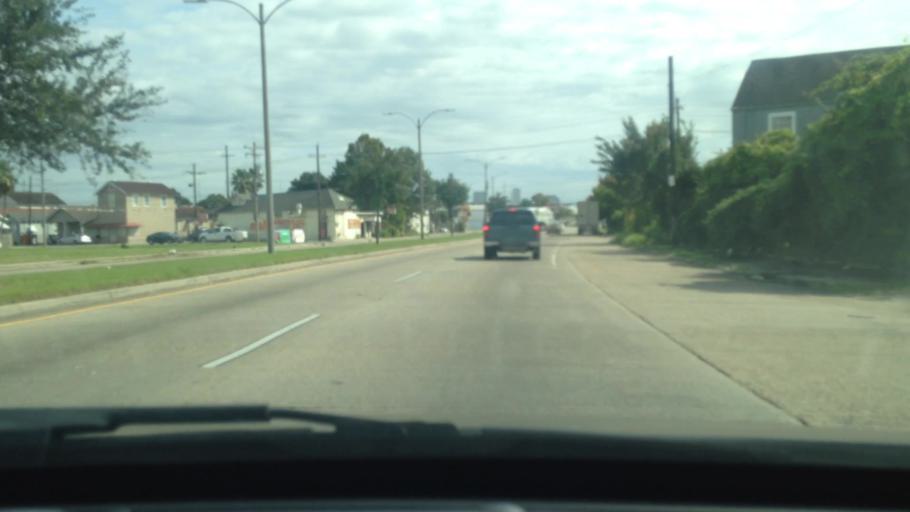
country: US
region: Louisiana
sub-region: Jefferson Parish
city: Jefferson
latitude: 29.9649
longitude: -90.1231
